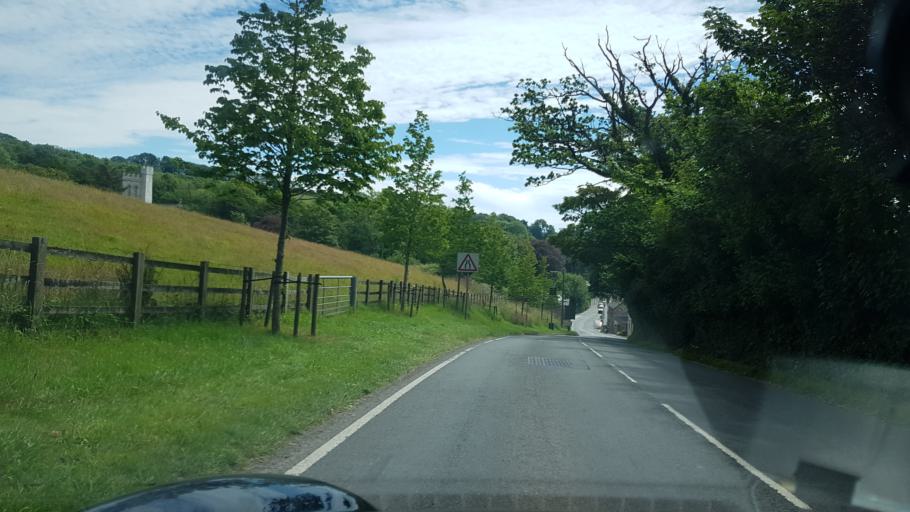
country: GB
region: Wales
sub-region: Carmarthenshire
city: Saint Clears
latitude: 51.7764
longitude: -4.4652
